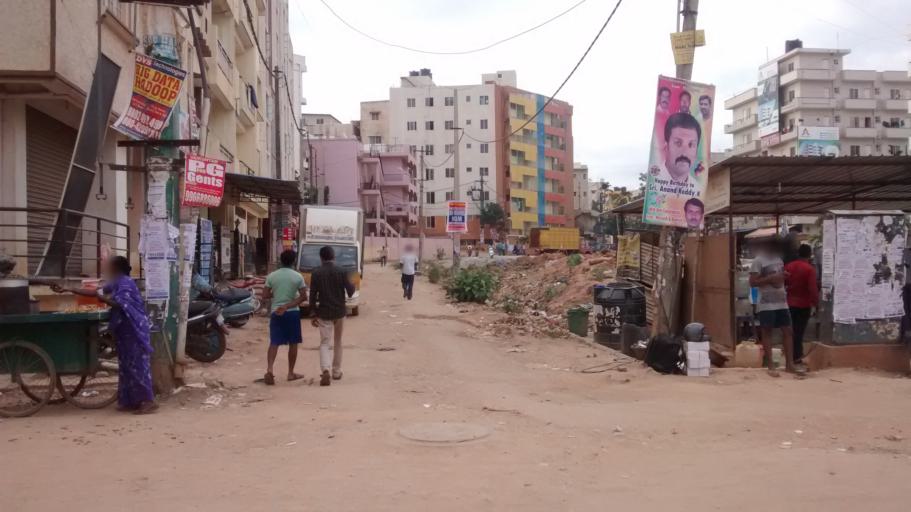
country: IN
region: Karnataka
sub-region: Bangalore Urban
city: Bangalore
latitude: 12.9508
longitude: 77.7038
